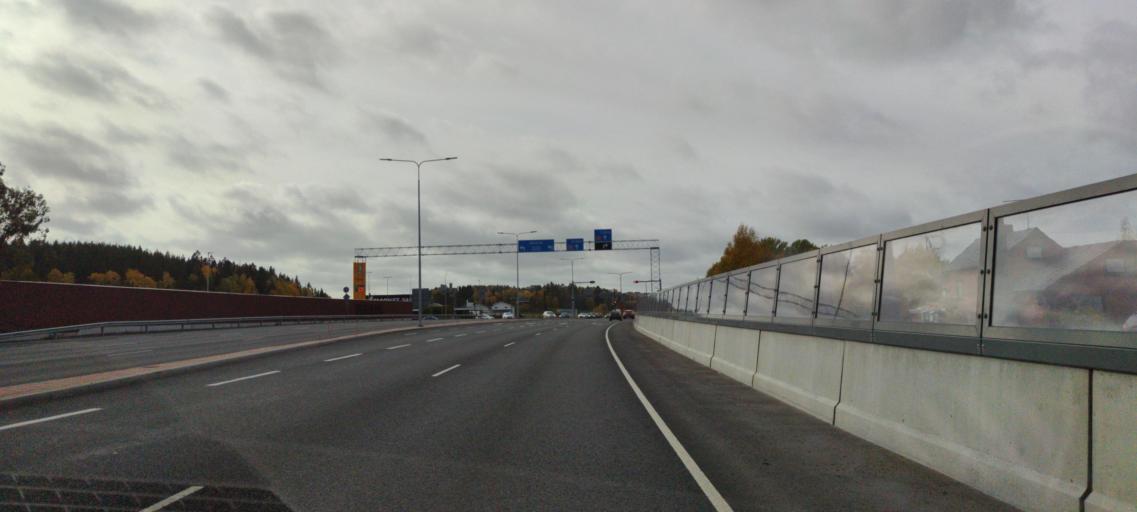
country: FI
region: Varsinais-Suomi
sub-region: Turku
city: Kaarina
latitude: 60.4678
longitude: 22.3502
